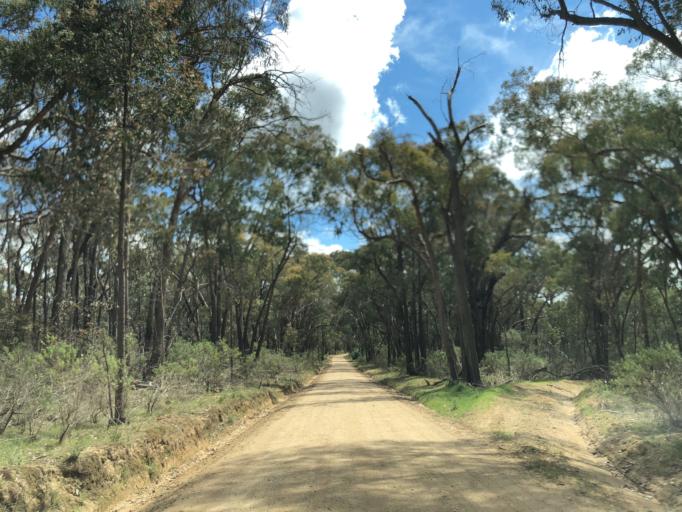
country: AU
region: Victoria
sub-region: Benalla
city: Benalla
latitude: -36.7361
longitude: 146.1506
